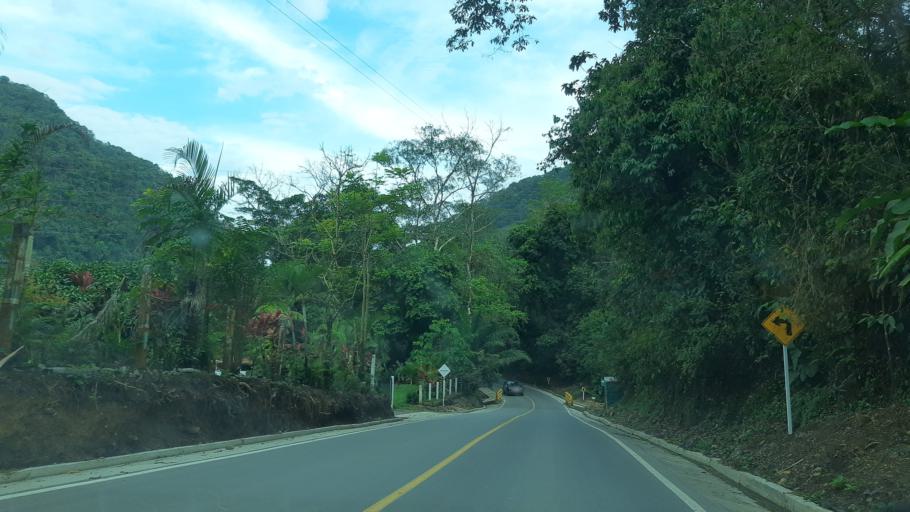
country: CO
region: Boyaca
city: Santa Maria
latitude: 4.8571
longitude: -73.2341
